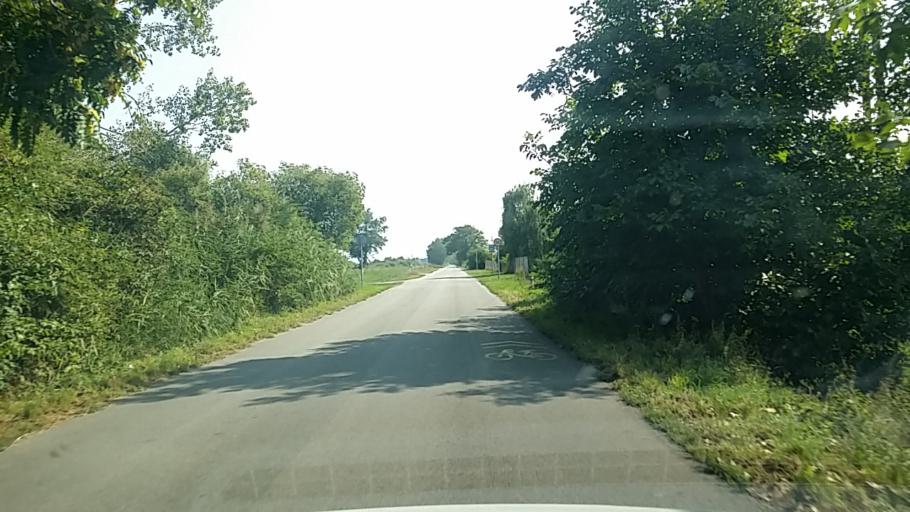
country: HU
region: Gyor-Moson-Sopron
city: Fertorakos
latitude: 47.7146
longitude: 16.6640
